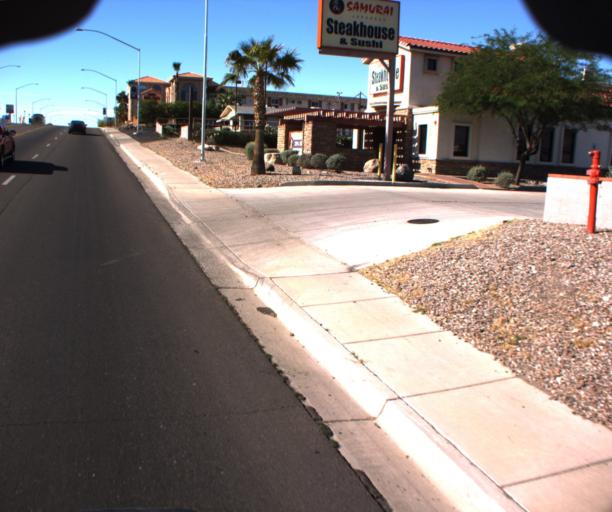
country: US
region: Arizona
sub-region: Mohave County
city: Bullhead City
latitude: 35.1146
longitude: -114.5982
